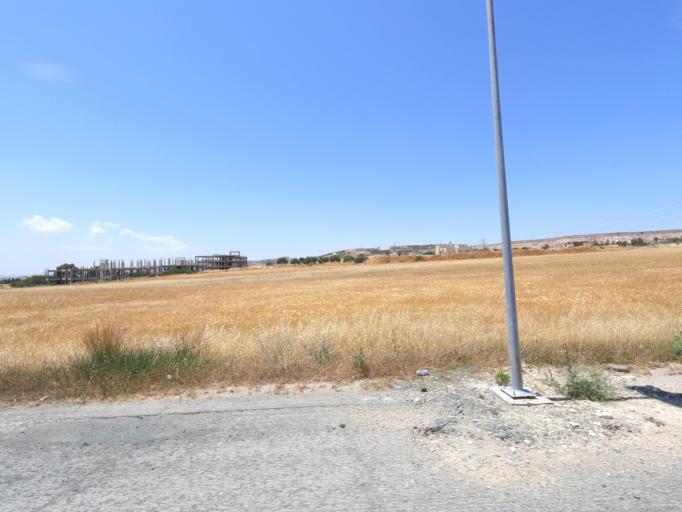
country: CY
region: Larnaka
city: Pyla
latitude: 35.0018
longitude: 33.6923
